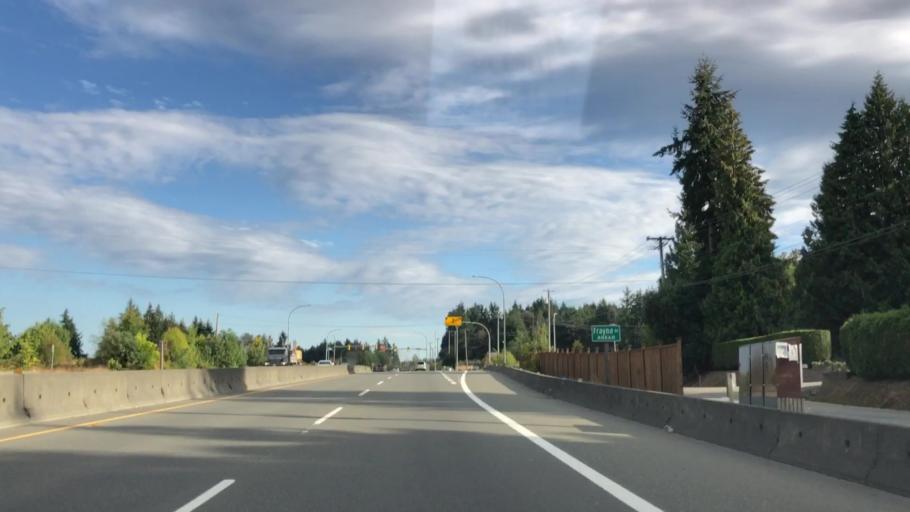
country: CA
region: British Columbia
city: North Saanich
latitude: 48.6439
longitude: -123.5554
